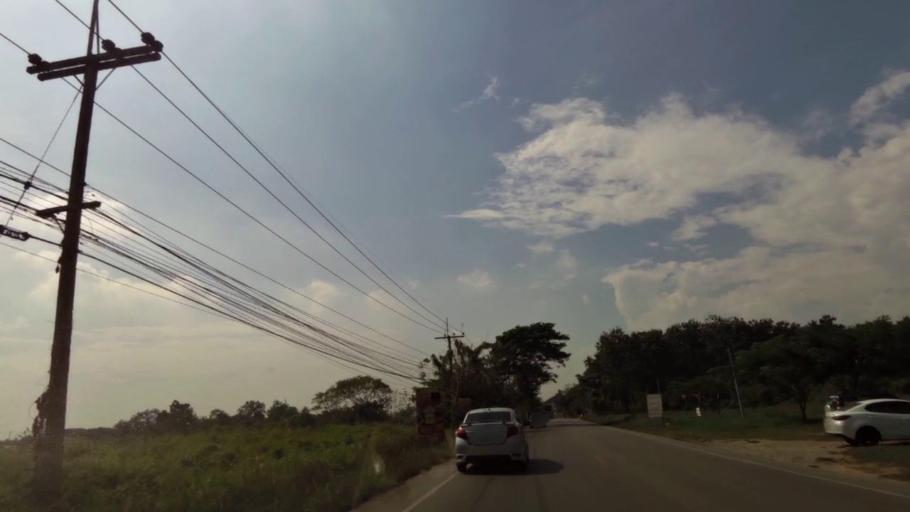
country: TH
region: Chiang Rai
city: Chiang Rai
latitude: 19.8641
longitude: 99.7719
